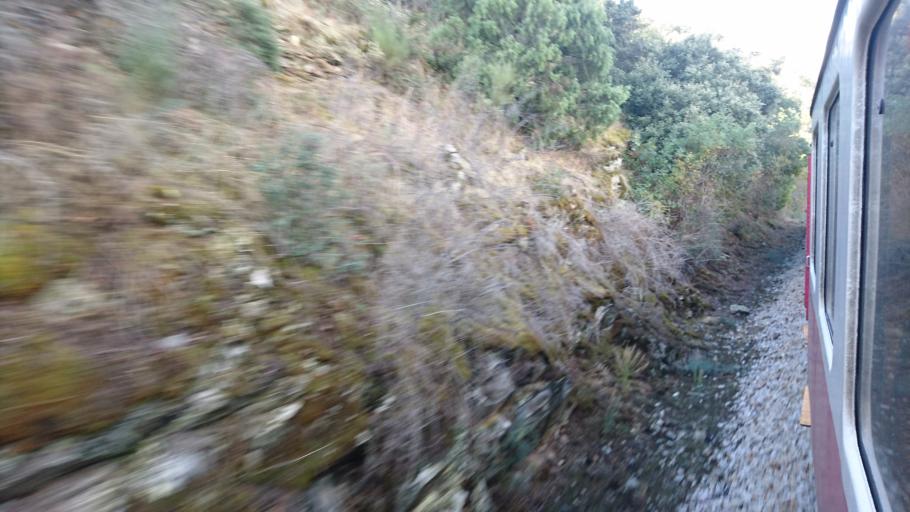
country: PT
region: Guarda
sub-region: Vila Nova de Foz Coa
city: Custoias
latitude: 41.1428
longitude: -7.2537
